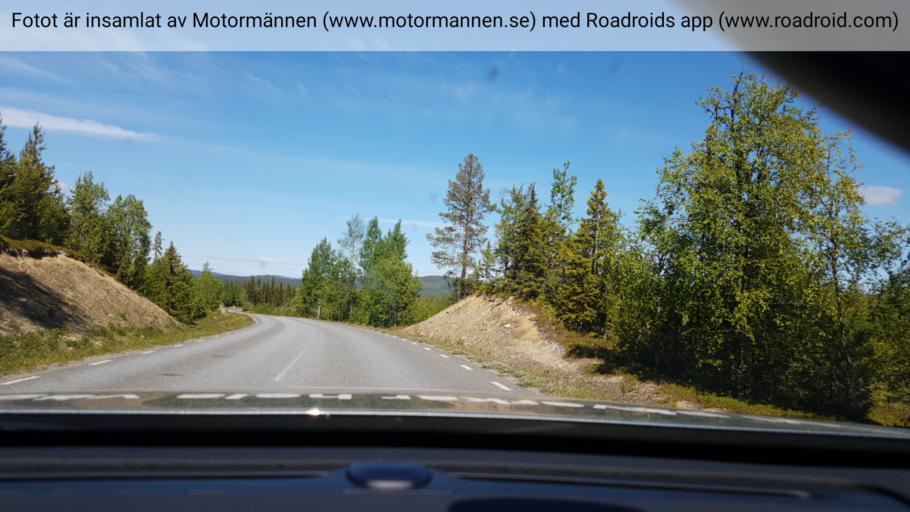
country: SE
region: Vaesterbotten
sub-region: Vilhelmina Kommun
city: Vilhelmina
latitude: 64.6463
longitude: 17.0795
